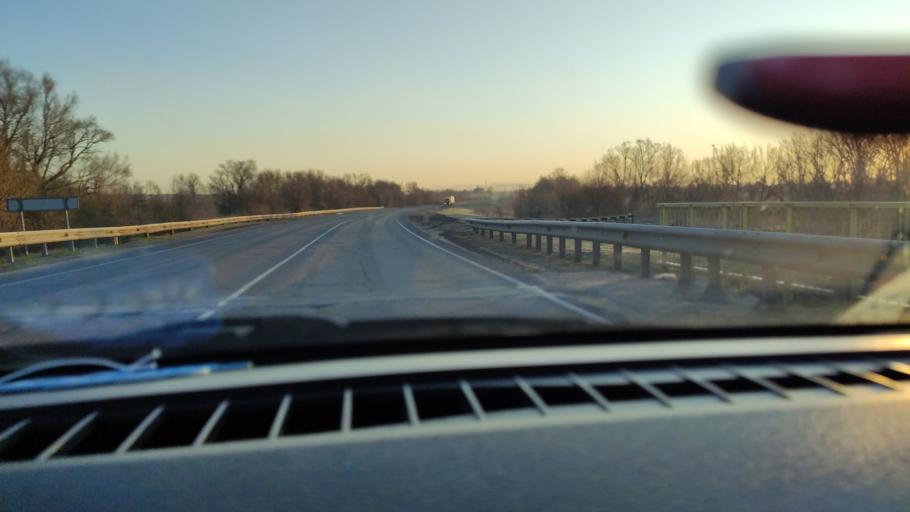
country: RU
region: Saratov
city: Sinodskoye
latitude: 51.9766
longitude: 46.6486
